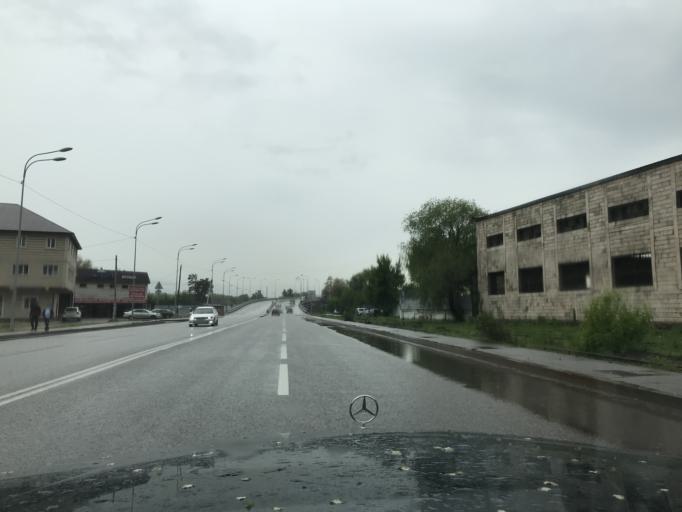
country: KZ
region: Almaty Oblysy
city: Pervomayskiy
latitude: 43.3412
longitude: 76.9664
